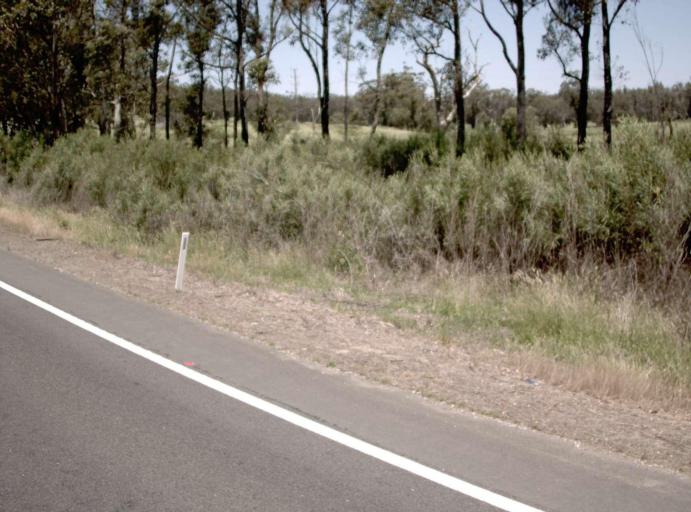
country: AU
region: Victoria
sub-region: East Gippsland
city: Lakes Entrance
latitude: -37.7531
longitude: 148.2958
